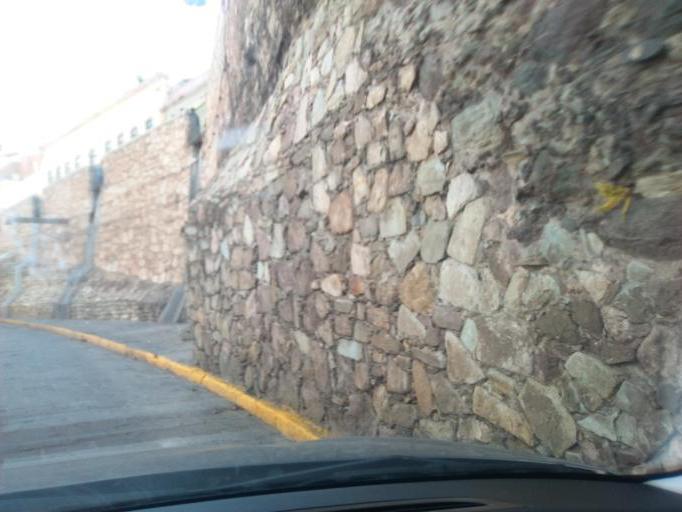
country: MX
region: Guanajuato
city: Guanajuato
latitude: 21.0194
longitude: -101.2604
